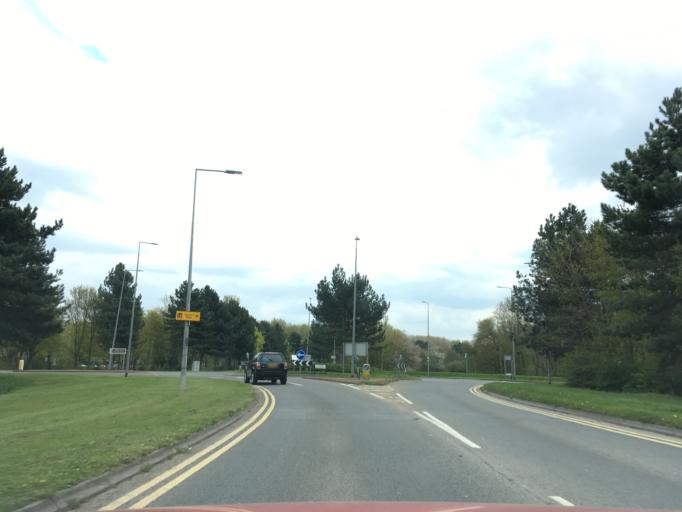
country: GB
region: England
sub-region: Milton Keynes
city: Milton Keynes
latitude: 52.0497
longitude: -0.7259
